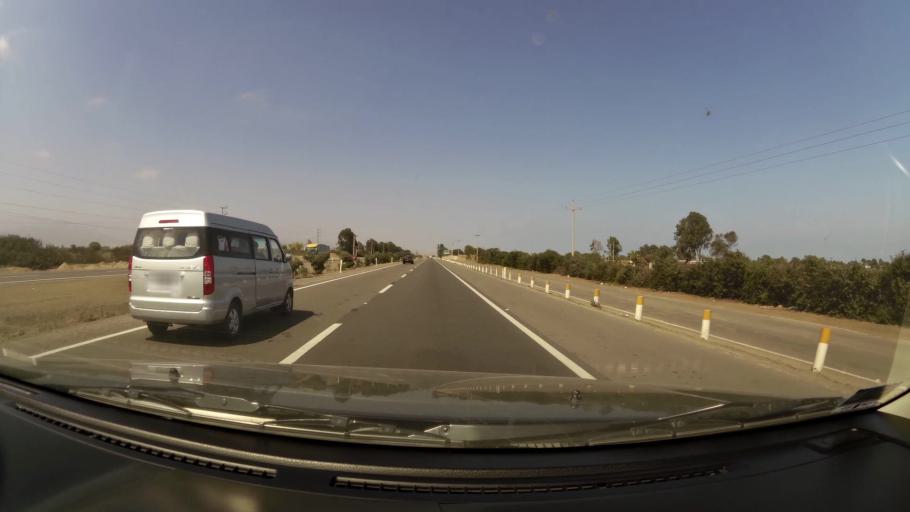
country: PE
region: Lima
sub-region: Provincia de Canete
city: Asia
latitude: -12.7703
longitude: -76.5927
